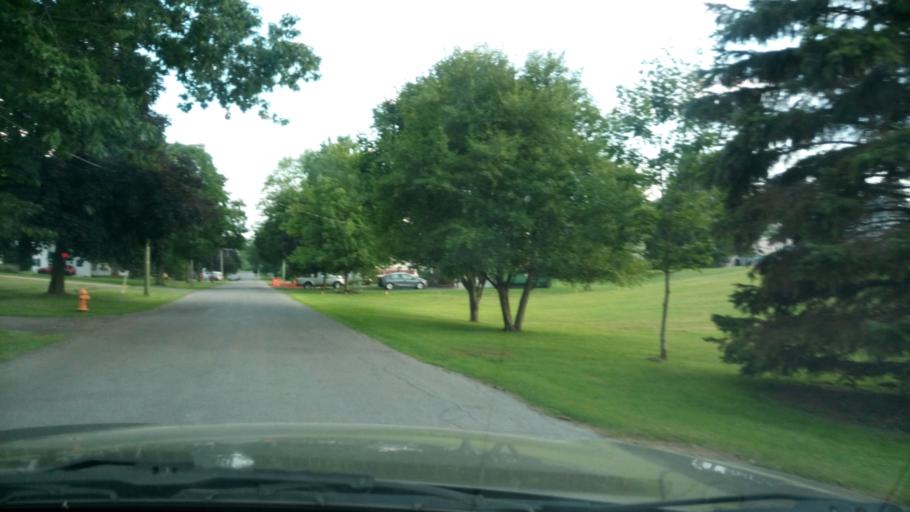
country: US
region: New York
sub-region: Wayne County
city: Clyde
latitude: 43.0888
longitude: -76.8792
